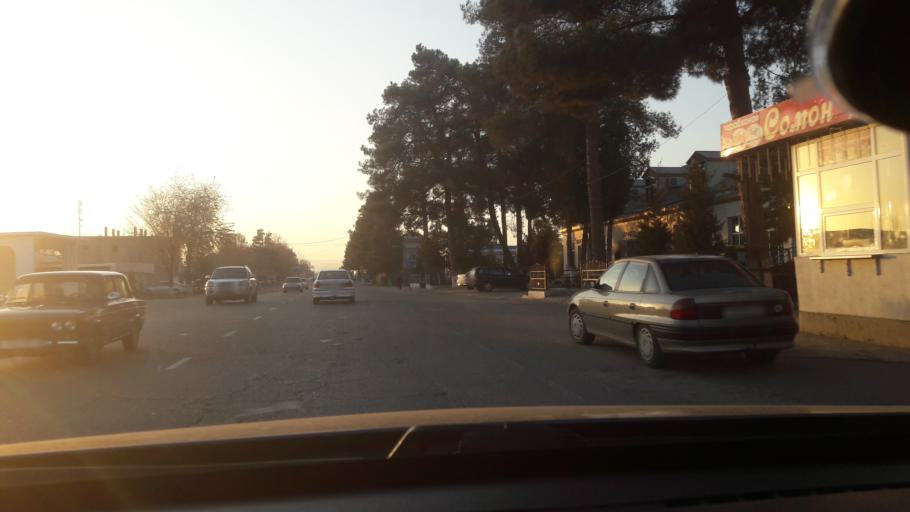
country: TJ
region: Khatlon
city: Vose'
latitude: 37.8053
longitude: 69.6256
